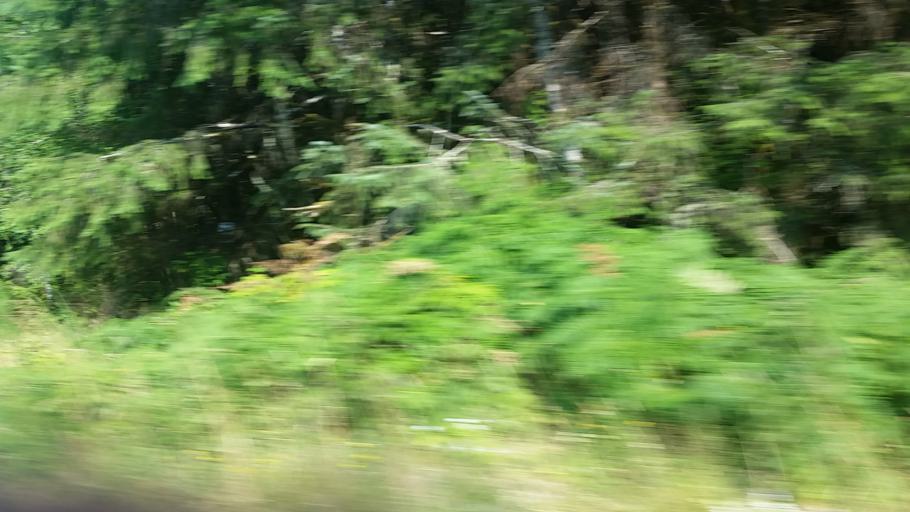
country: US
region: Washington
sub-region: Clallam County
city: Forks
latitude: 47.9514
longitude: -124.4617
